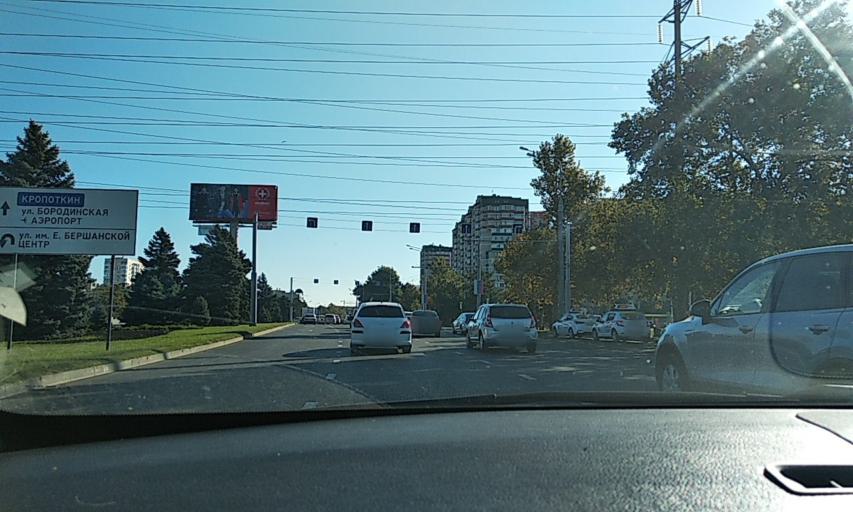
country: RU
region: Krasnodarskiy
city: Pashkovskiy
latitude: 45.0124
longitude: 39.0657
